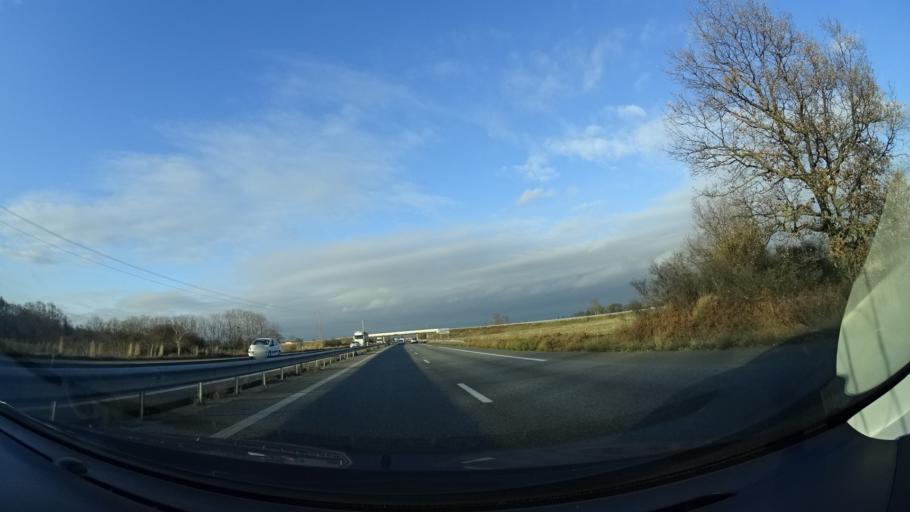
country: FR
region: Midi-Pyrenees
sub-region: Departement de l'Ariege
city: Saint-Jean-du-Falga
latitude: 43.0914
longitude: 1.6340
